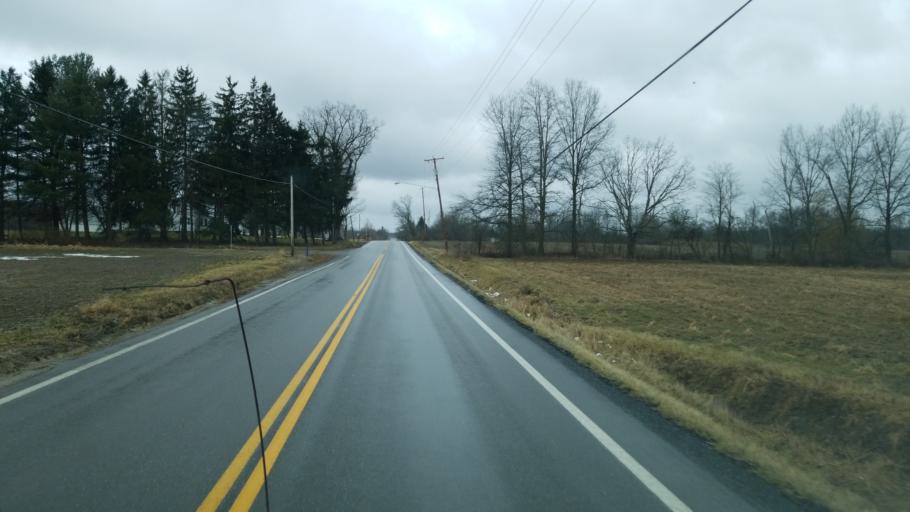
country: US
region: Ohio
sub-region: Trumbull County
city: Champion Heights
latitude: 41.3606
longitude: -80.9546
